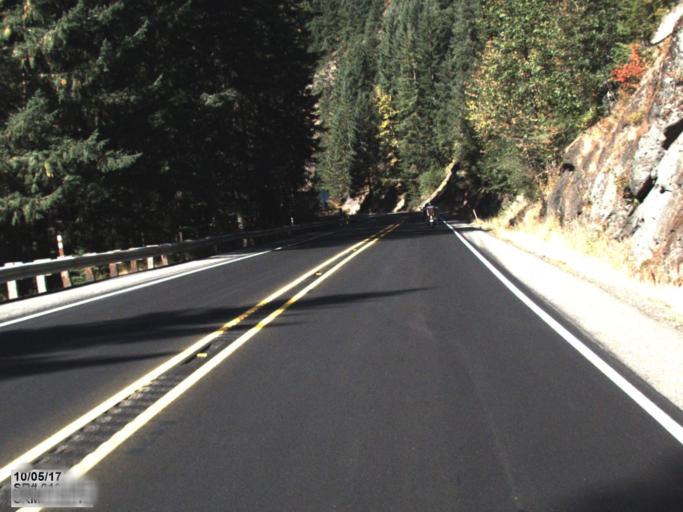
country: US
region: Washington
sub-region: Pierce County
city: Buckley
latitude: 46.6782
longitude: -121.5301
